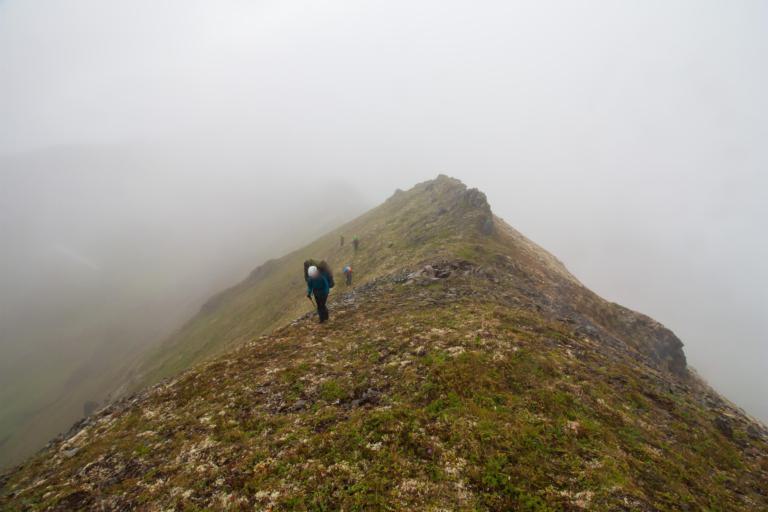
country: RU
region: Kamtsjatka
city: Yelizovo
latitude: 54.0105
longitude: 158.0837
